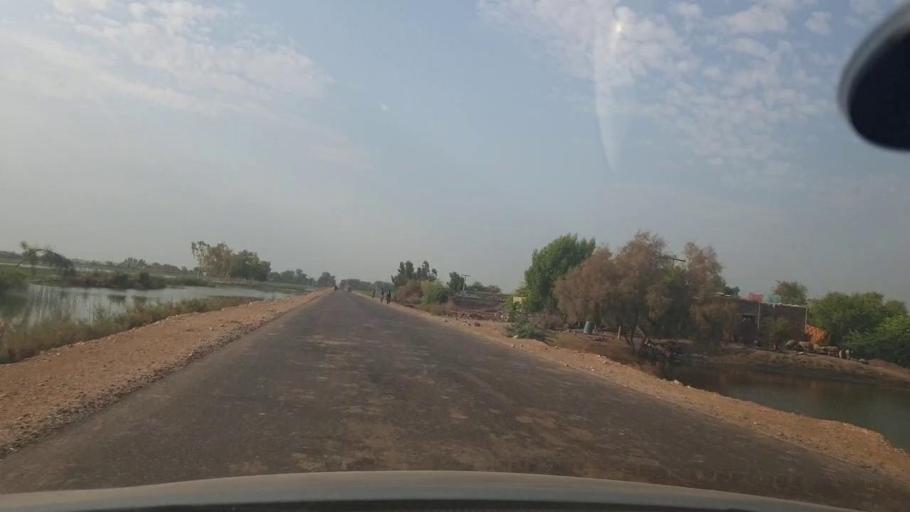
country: PK
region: Sindh
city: Jacobabad
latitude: 28.1178
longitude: 68.3273
